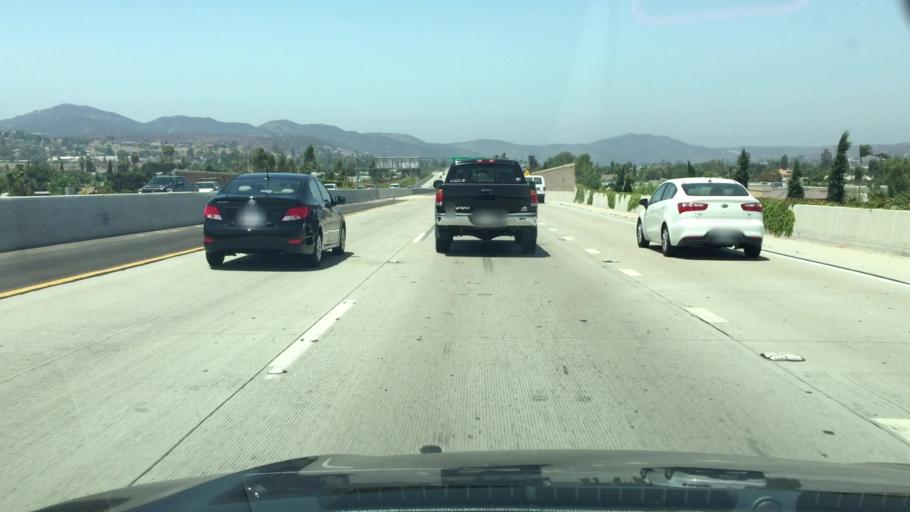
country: US
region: California
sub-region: San Diego County
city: Santee
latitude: 32.8329
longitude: -116.9727
